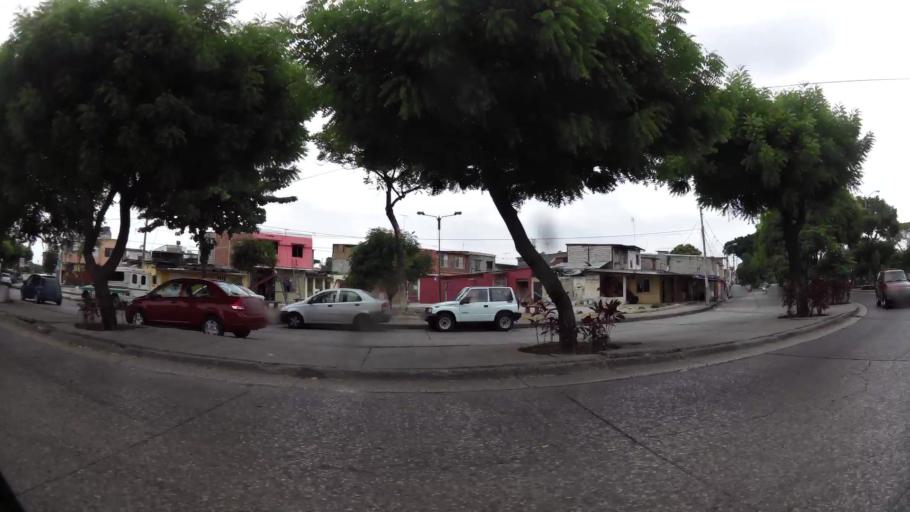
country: EC
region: Guayas
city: Eloy Alfaro
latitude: -2.1247
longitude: -79.8896
